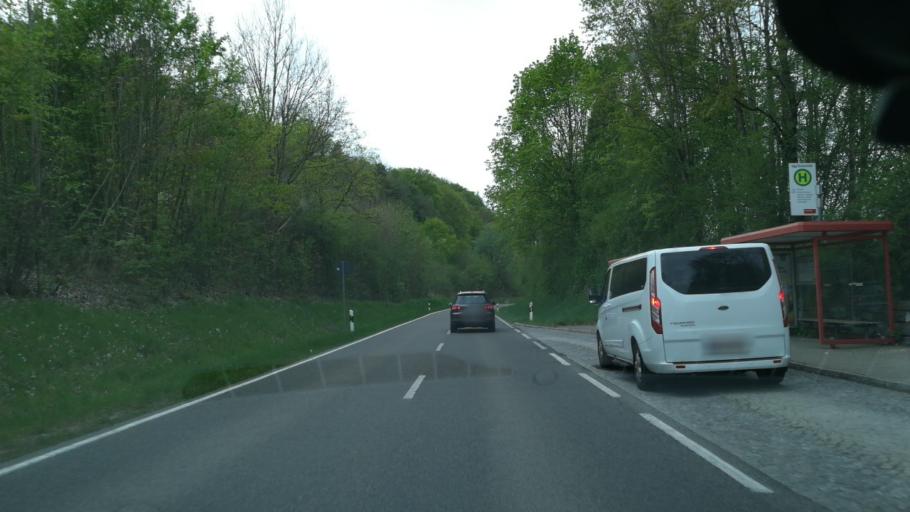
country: DE
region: Baden-Wuerttemberg
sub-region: Freiburg Region
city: Konstanz
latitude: 47.6916
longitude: 9.1905
